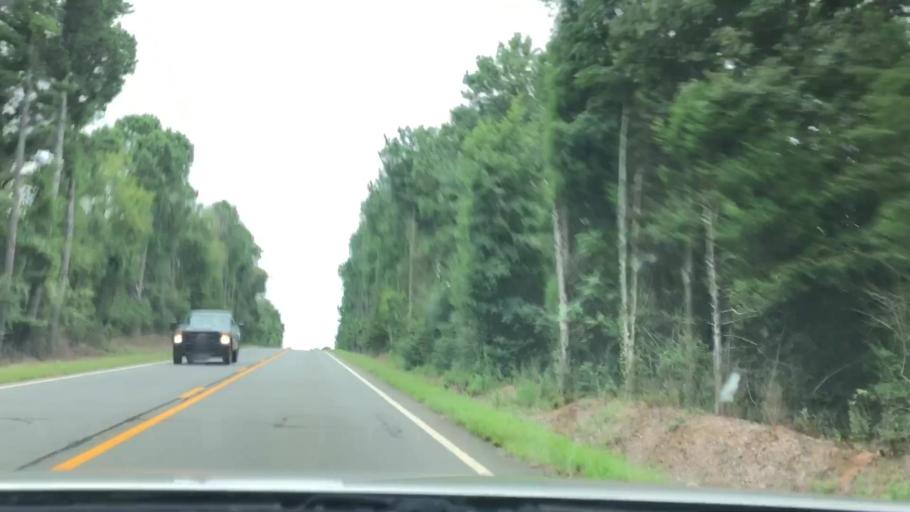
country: US
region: Georgia
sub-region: Pike County
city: Zebulon
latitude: 33.0769
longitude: -84.4539
